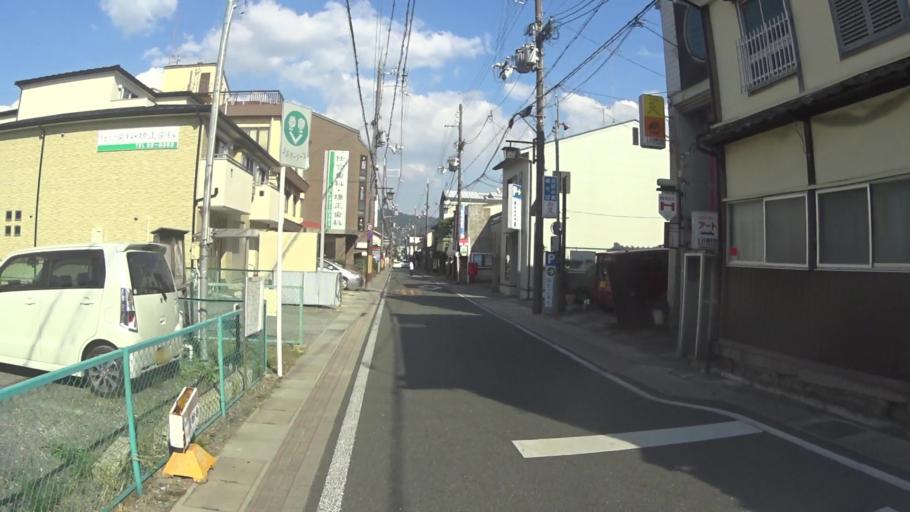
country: JP
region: Kyoto
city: Kameoka
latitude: 35.0099
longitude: 135.5807
